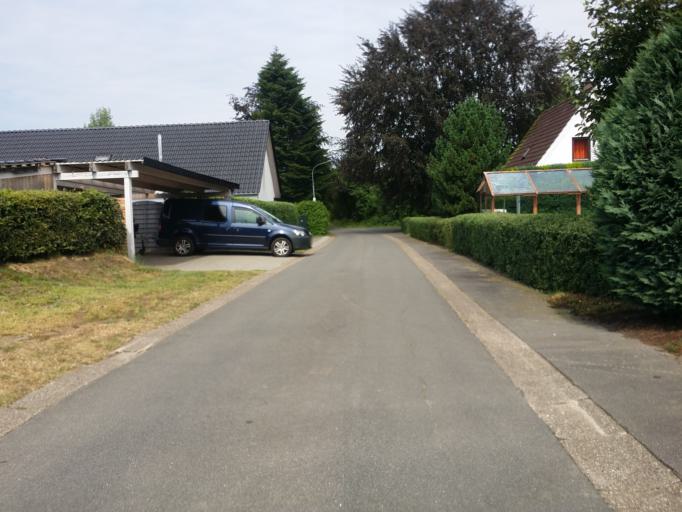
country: DE
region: Schleswig-Holstein
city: Vaale
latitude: 54.0107
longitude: 9.3853
